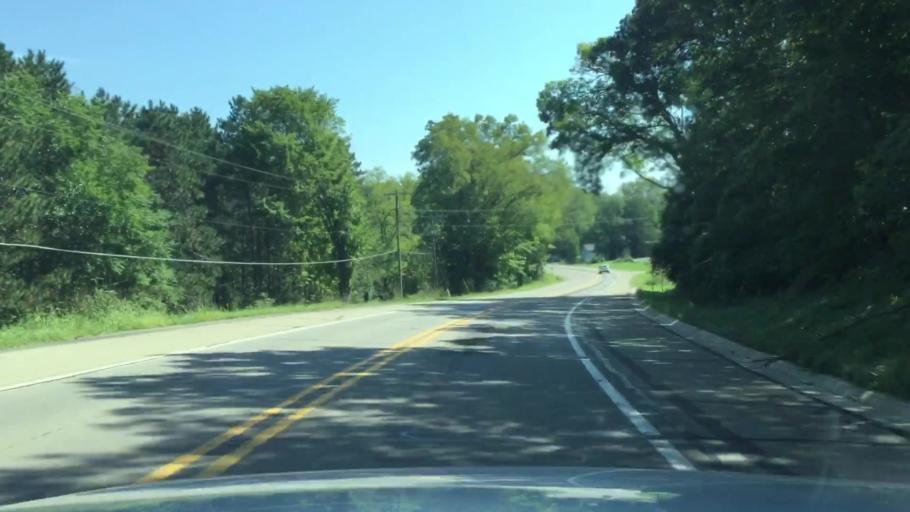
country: US
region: Michigan
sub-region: Jackson County
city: Brooklyn
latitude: 42.0570
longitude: -84.1513
